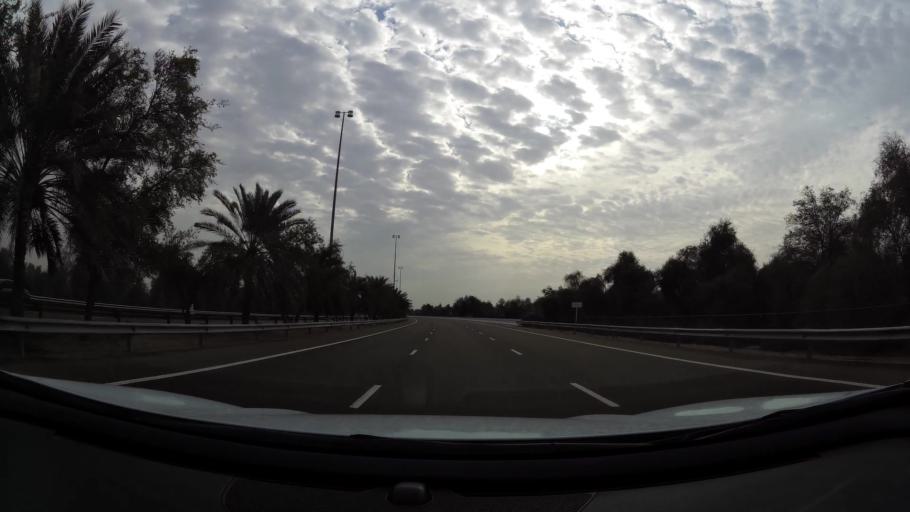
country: AE
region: Abu Dhabi
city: Al Ain
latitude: 24.1708
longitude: 55.2211
